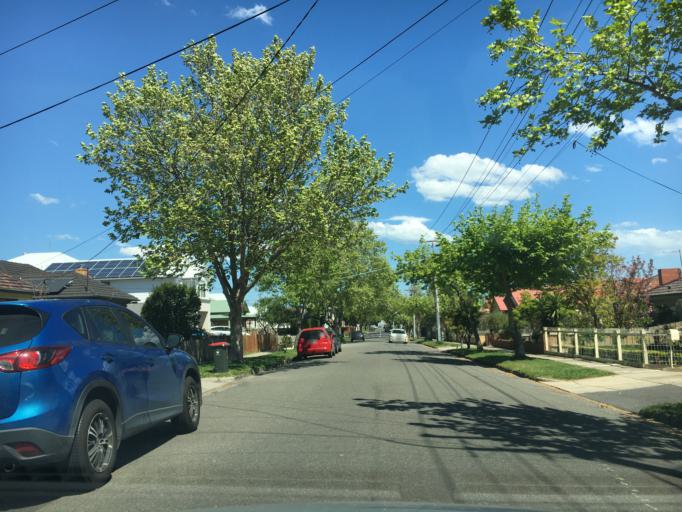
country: AU
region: Victoria
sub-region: Monash
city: Chadstone
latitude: -37.9020
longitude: 145.1023
